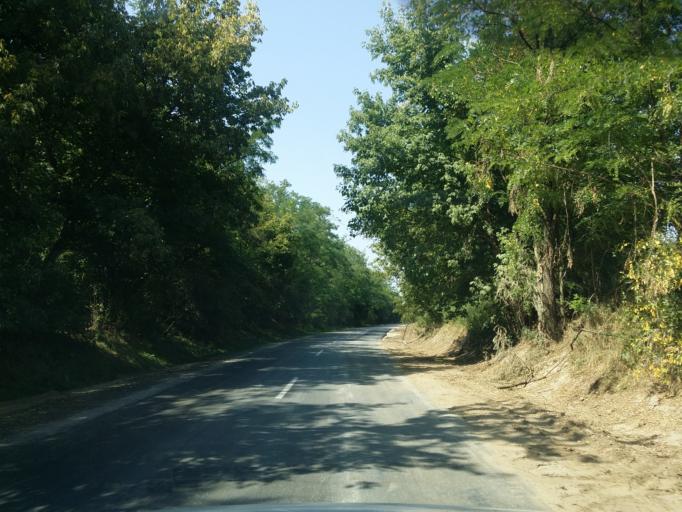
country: HU
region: Tolna
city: Pincehely
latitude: 46.6229
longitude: 18.4166
